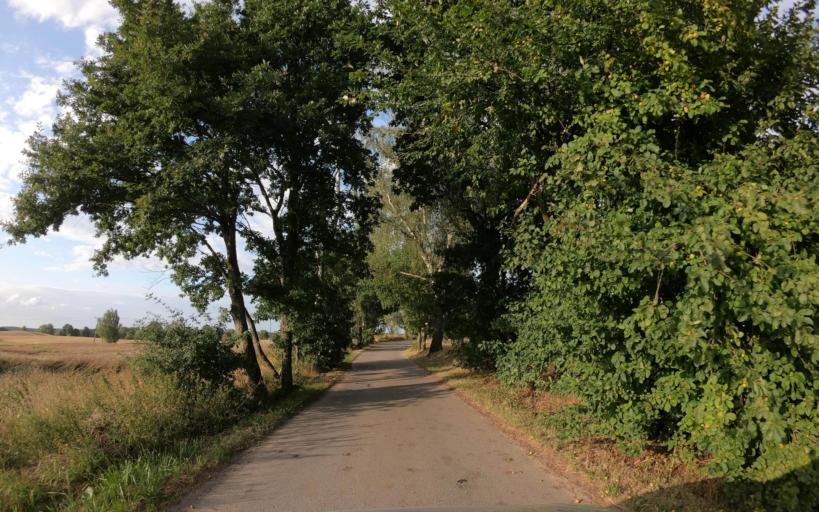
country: PL
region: West Pomeranian Voivodeship
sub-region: Powiat drawski
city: Czaplinek
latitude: 53.5485
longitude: 16.1642
